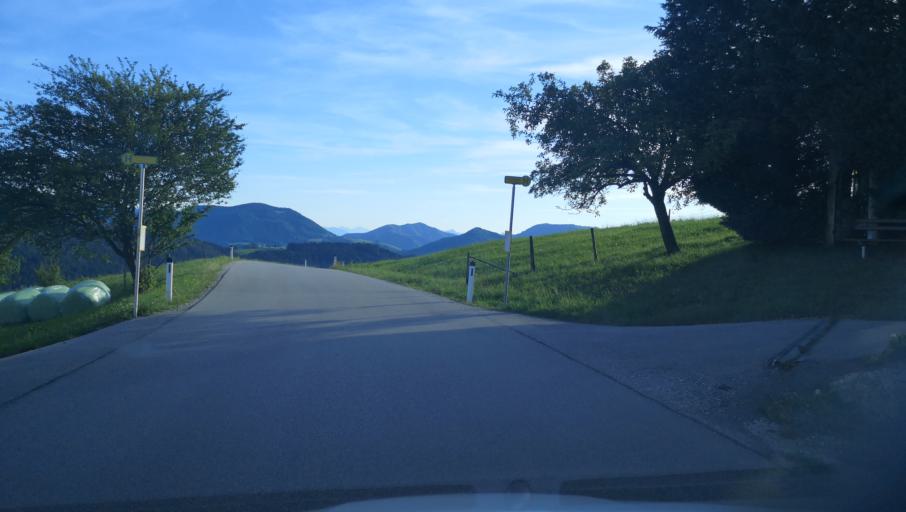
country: AT
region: Lower Austria
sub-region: Waidhofen an der Ybbs Stadt
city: Waidhofen an der Ybbs
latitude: 47.9778
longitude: 14.8304
